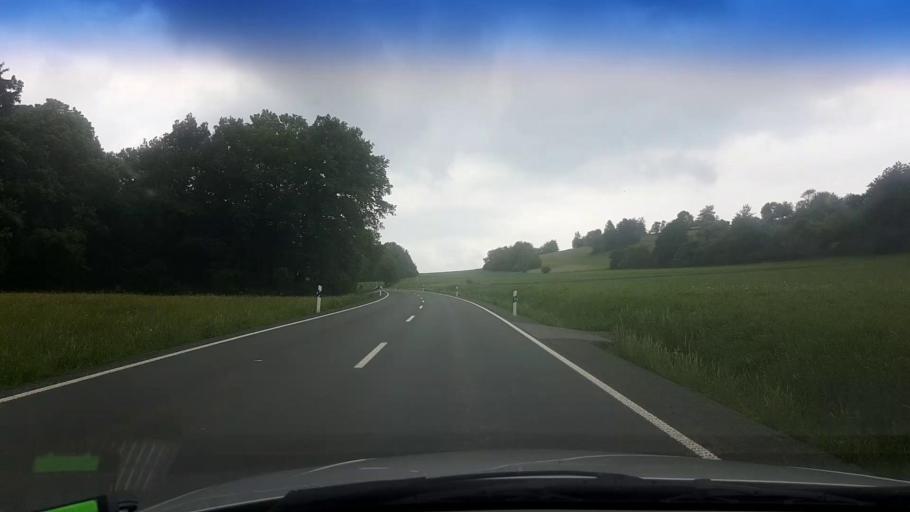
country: DE
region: Bavaria
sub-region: Upper Franconia
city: Reuth
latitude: 49.9882
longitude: 11.6879
